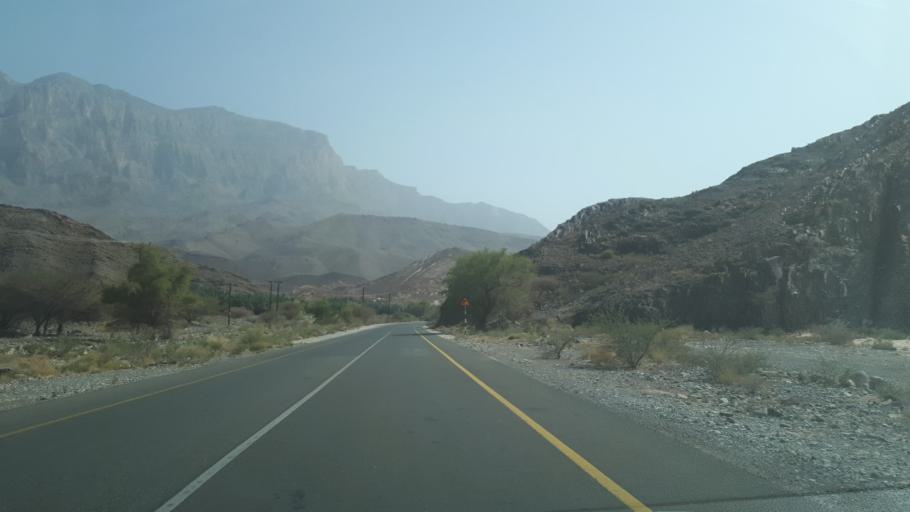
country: OM
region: Muhafazat ad Dakhiliyah
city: Bahla'
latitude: 23.2160
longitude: 57.0253
